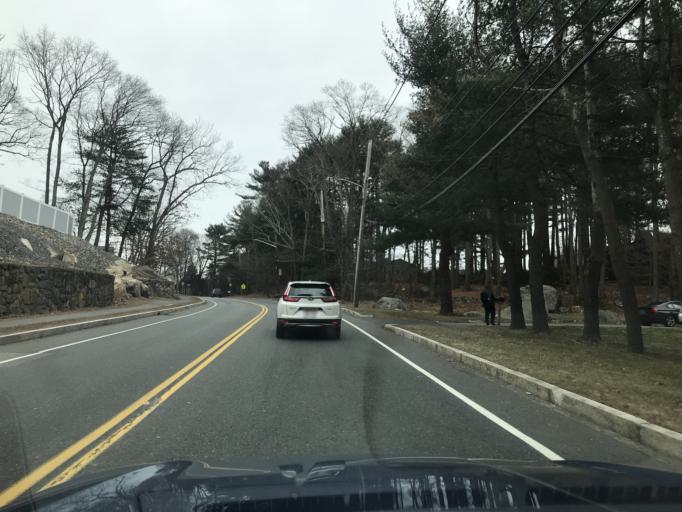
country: US
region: Massachusetts
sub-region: Essex County
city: Lynnfield
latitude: 42.5129
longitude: -71.0185
